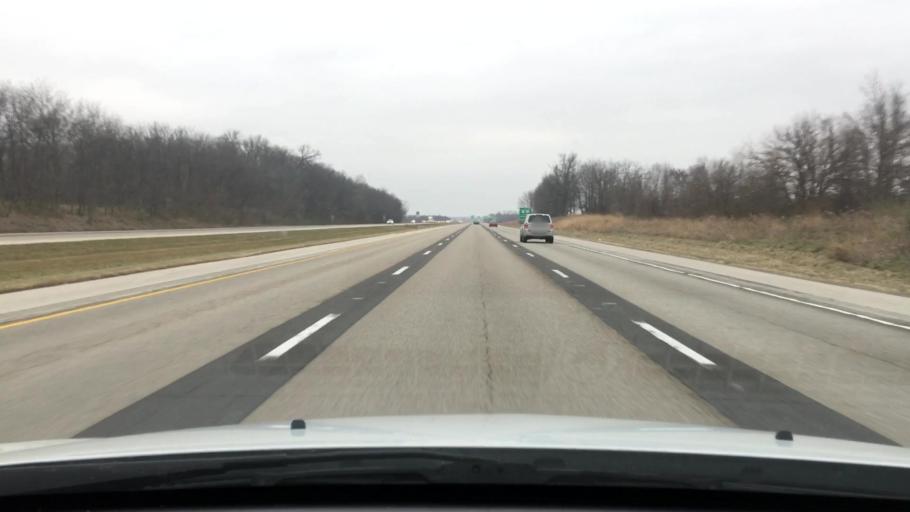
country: US
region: Illinois
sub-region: Logan County
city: Lincoln
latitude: 40.1506
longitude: -89.4172
